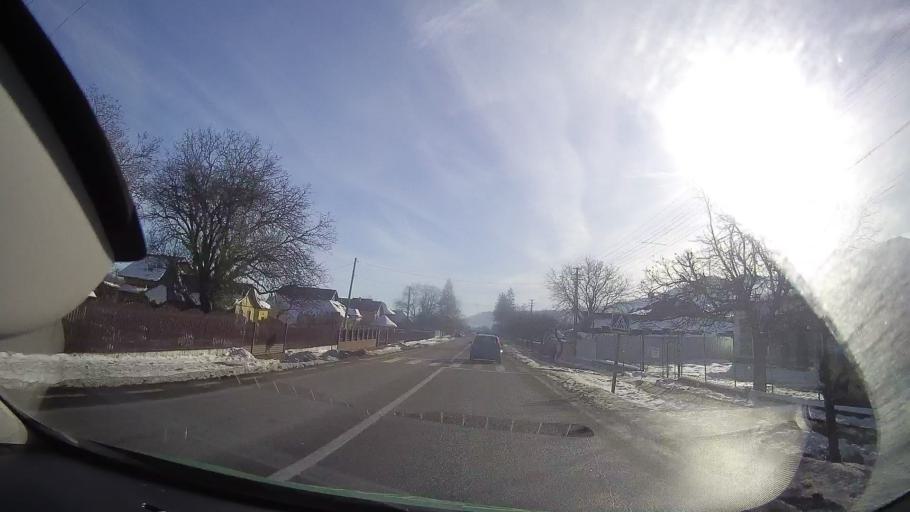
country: RO
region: Neamt
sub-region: Comuna Cracaoani
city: Cracaoani
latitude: 47.0998
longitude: 26.3089
